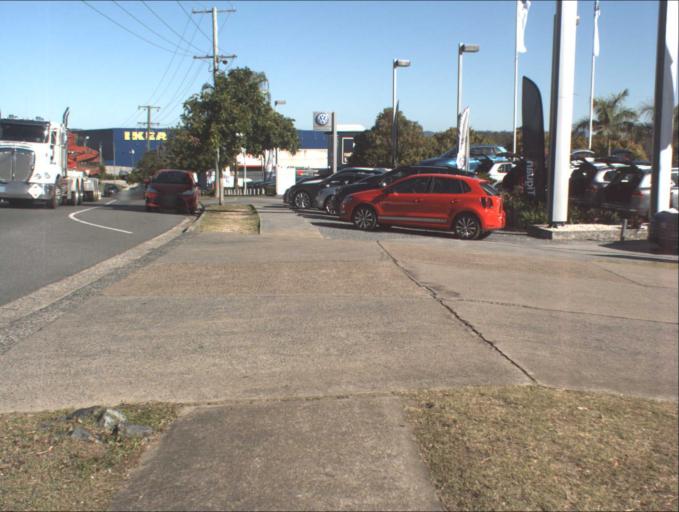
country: AU
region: Queensland
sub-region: Logan
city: Springwood
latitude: -27.6336
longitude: 153.1316
